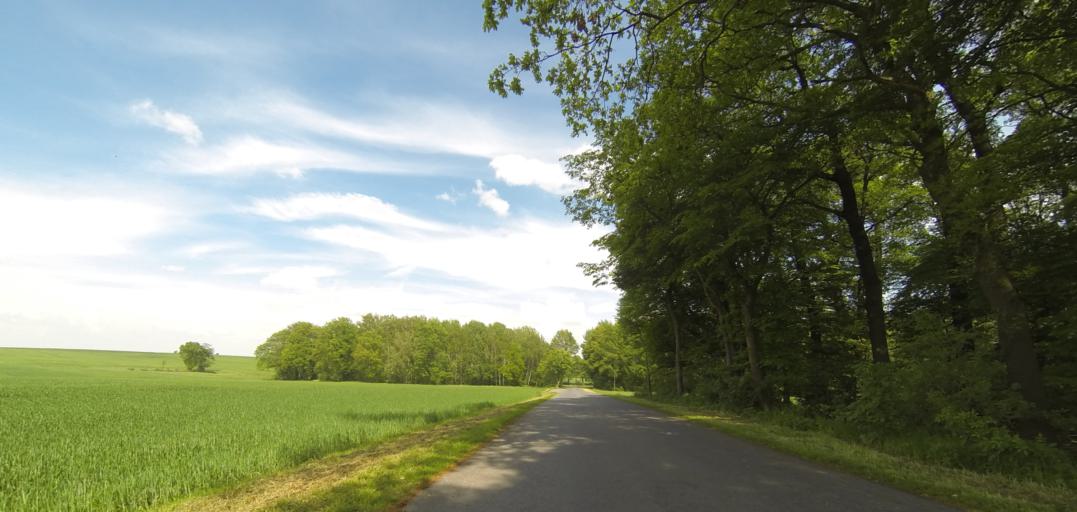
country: DE
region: Saxony
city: Radeberg
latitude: 51.0830
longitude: 13.9438
